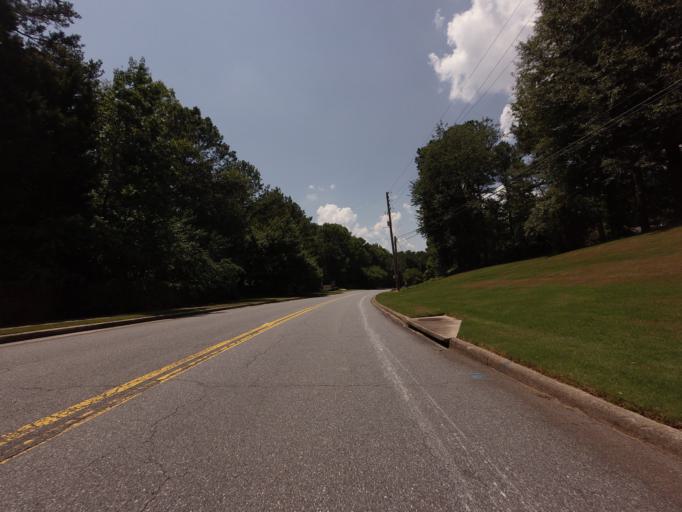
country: US
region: Georgia
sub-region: Fulton County
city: Johns Creek
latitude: 34.0407
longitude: -84.1907
